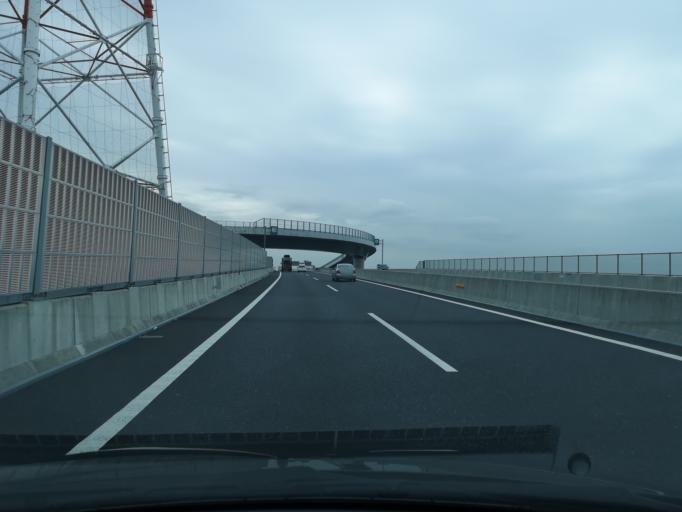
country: JP
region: Kanagawa
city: Atsugi
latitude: 35.4078
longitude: 139.3729
